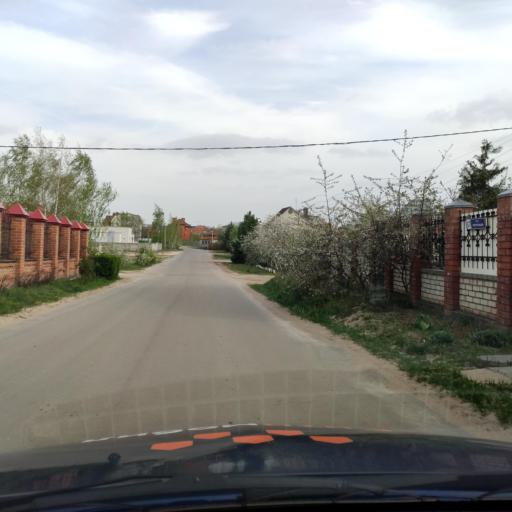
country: RU
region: Voronezj
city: Pridonskoy
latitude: 51.6436
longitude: 39.0852
